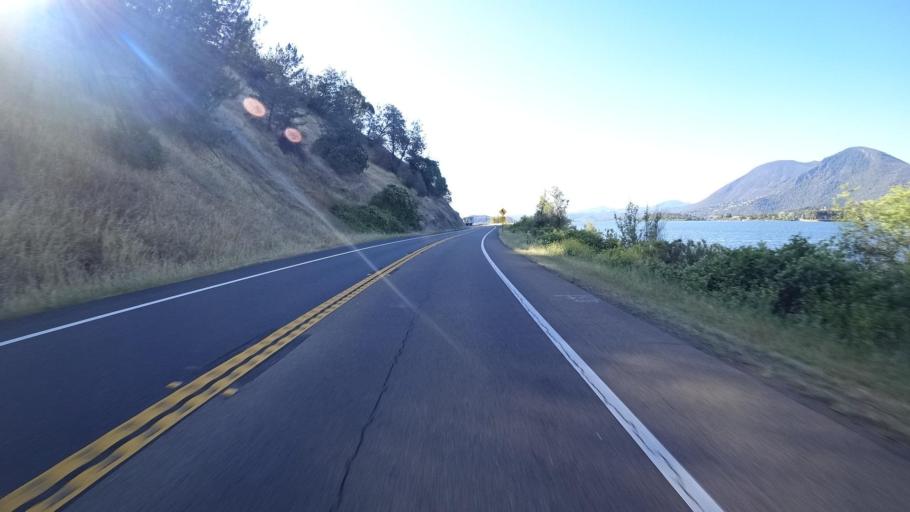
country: US
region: California
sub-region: Lake County
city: Soda Bay
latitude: 39.0350
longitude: -122.7449
